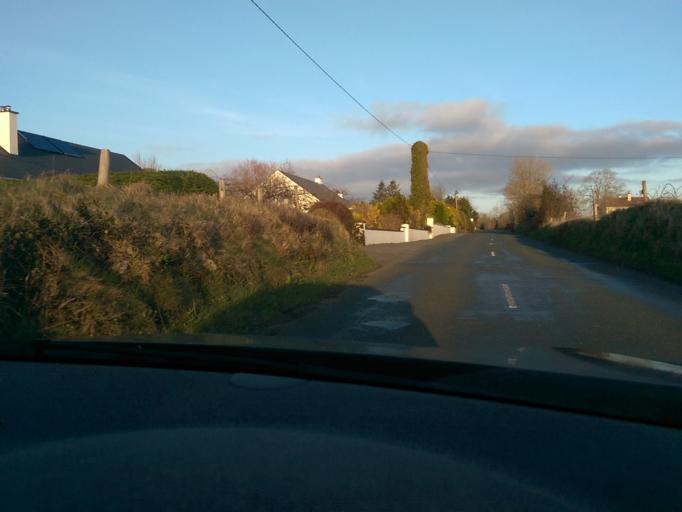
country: IE
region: Connaught
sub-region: Sligo
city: Tobercurry
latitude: 54.0510
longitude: -8.7045
